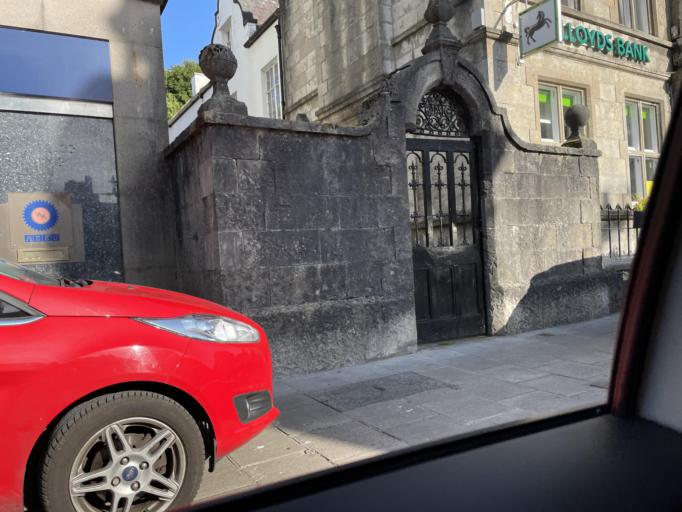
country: GB
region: Wales
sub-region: Gwynedd
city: Bangor
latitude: 53.2275
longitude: -4.1246
